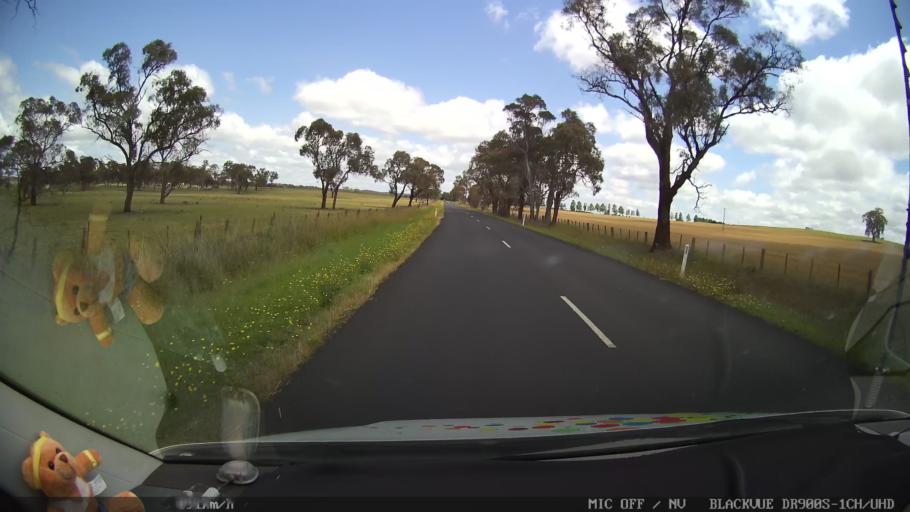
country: AU
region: New South Wales
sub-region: Glen Innes Severn
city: Glen Innes
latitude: -29.6510
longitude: 151.6932
